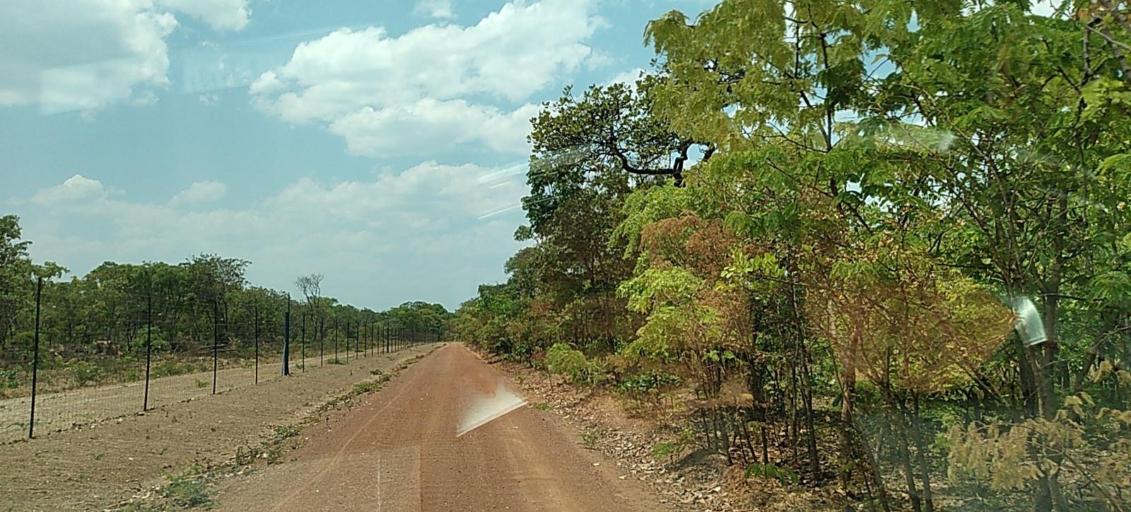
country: ZM
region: Copperbelt
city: Chililabombwe
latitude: -12.5174
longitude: 27.6266
